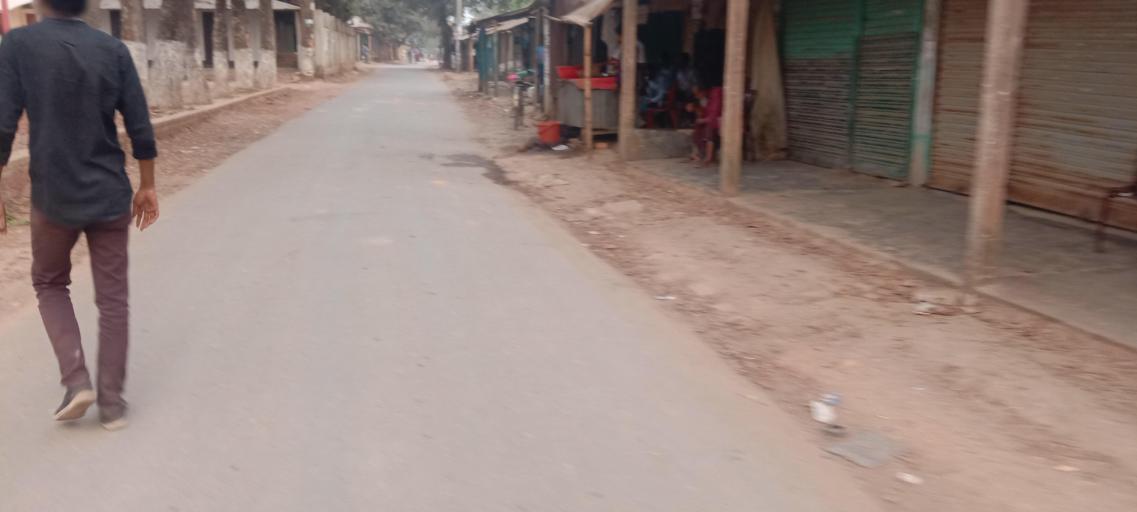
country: BD
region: Dhaka
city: Gafargaon
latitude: 24.3917
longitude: 90.4267
